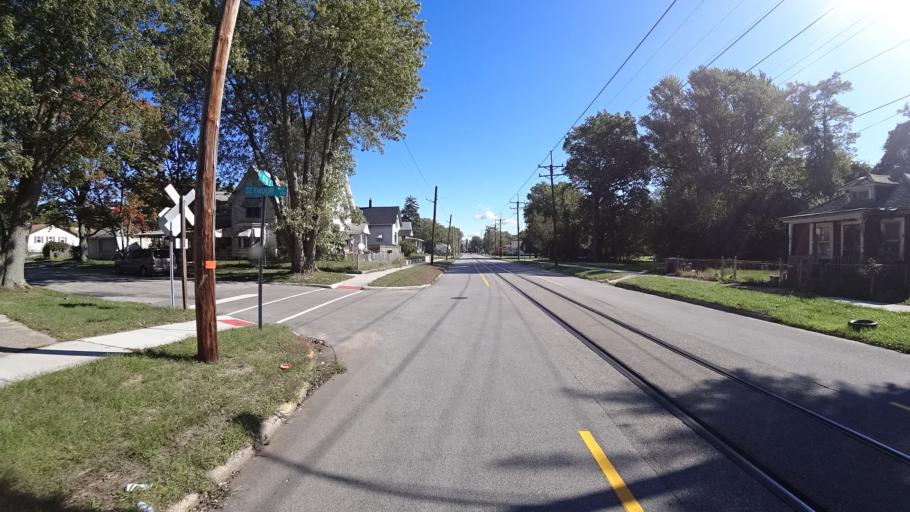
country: US
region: Indiana
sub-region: LaPorte County
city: Michigan City
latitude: 41.7075
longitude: -86.9171
